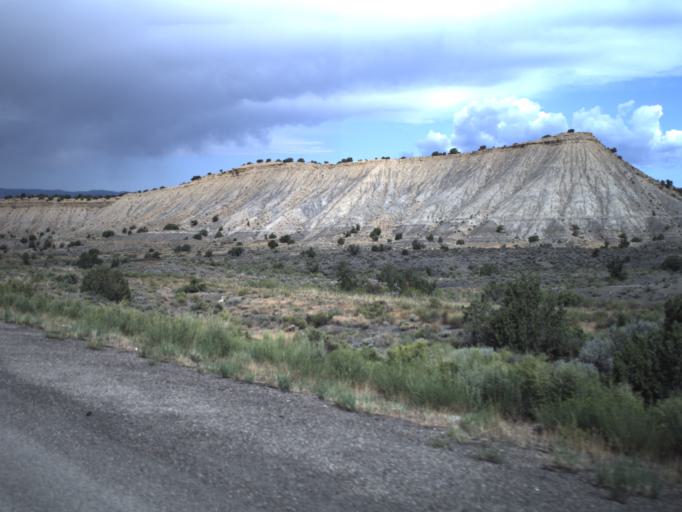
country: US
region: Utah
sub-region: Carbon County
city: Wellington
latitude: 39.5470
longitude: -110.6391
